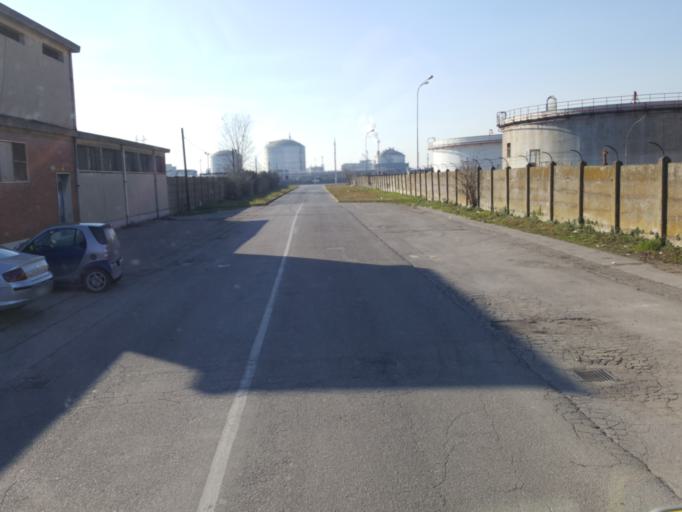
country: IT
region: Veneto
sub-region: Provincia di Venezia
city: Mestre
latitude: 45.4590
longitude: 12.2386
